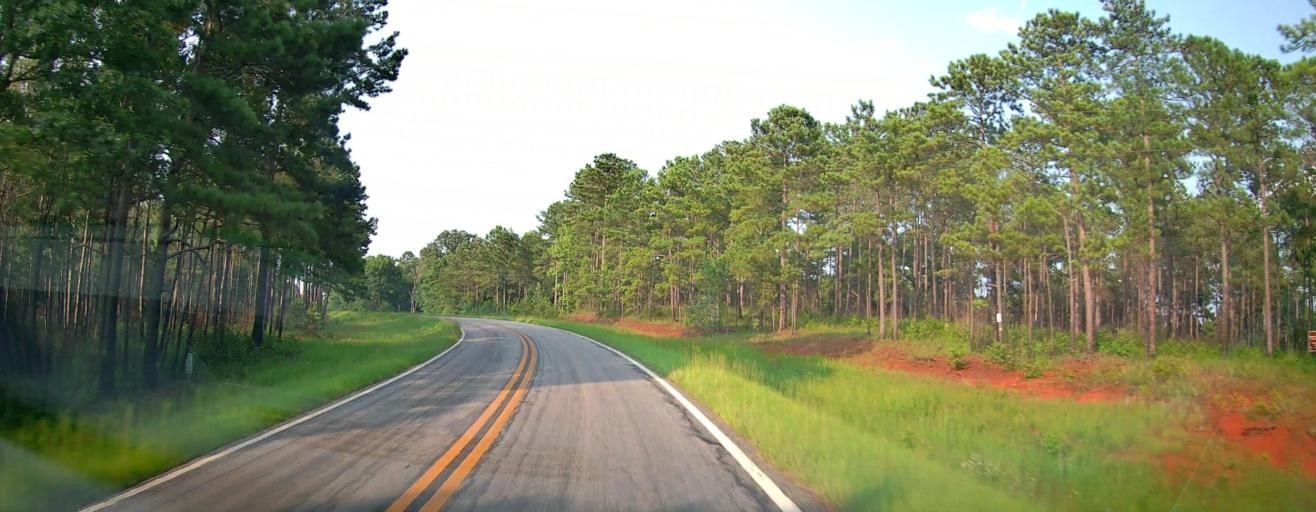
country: US
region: Georgia
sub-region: Jones County
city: Gray
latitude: 33.1071
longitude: -83.6604
